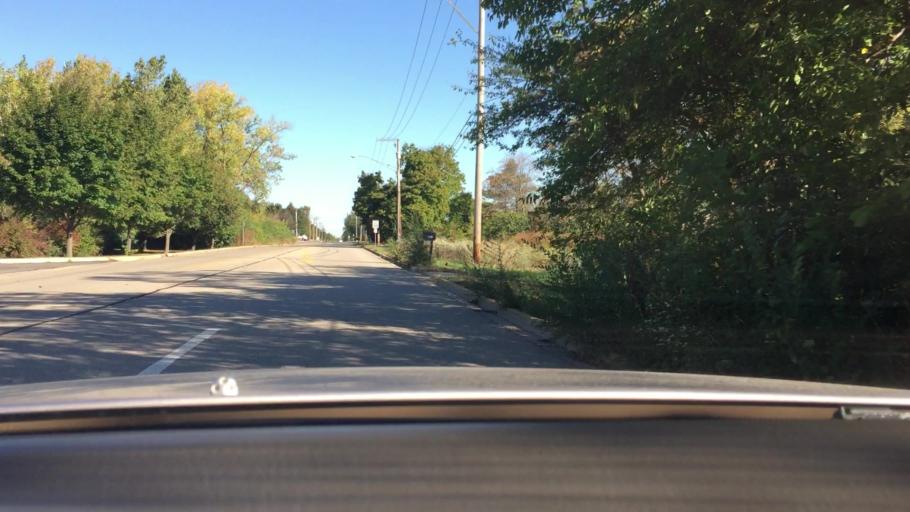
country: US
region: Illinois
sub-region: Lake County
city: Forest Lake
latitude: 42.1984
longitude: -88.0676
